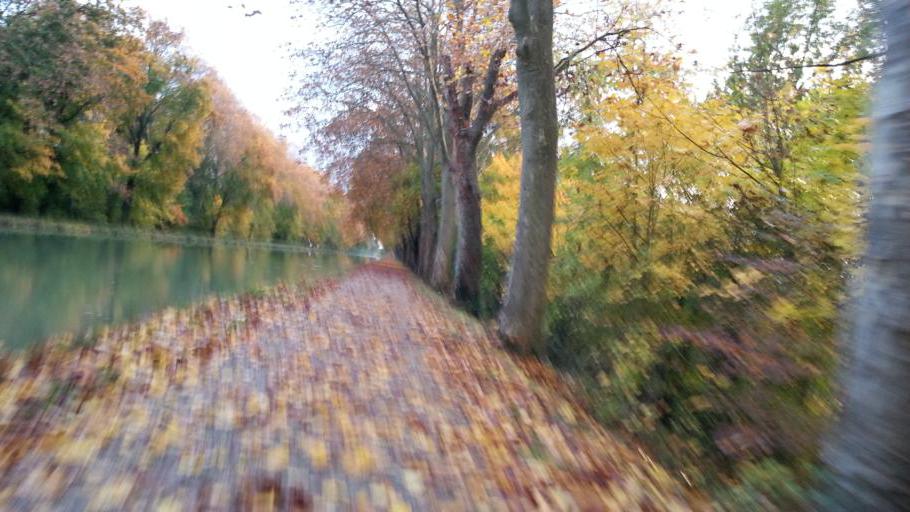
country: FR
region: Midi-Pyrenees
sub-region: Departement du Tarn-et-Garonne
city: Moissac
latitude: 44.0834
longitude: 1.1002
